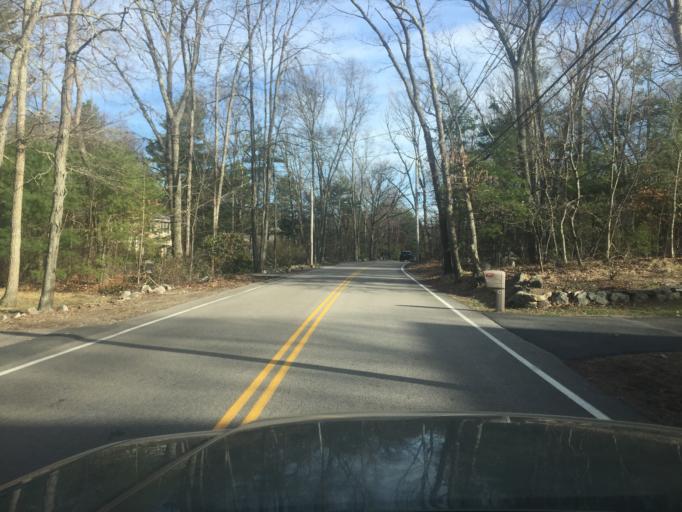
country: US
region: Massachusetts
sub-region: Worcester County
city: Milford
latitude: 42.1447
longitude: -71.4683
